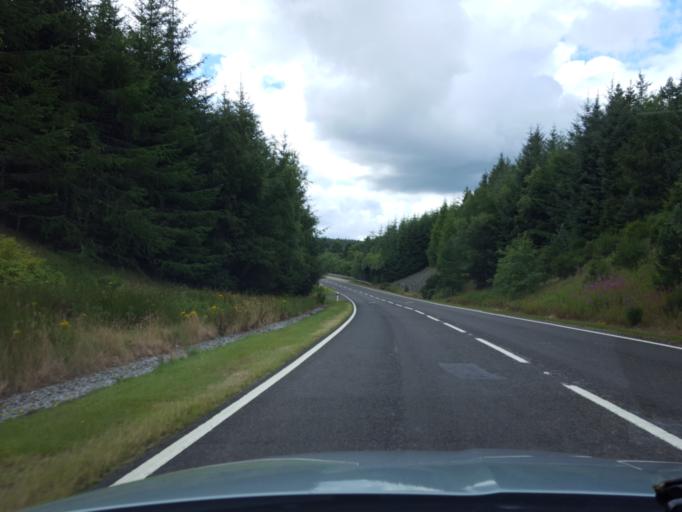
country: GB
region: Scotland
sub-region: Highland
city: Grantown on Spey
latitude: 57.3029
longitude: -3.6587
